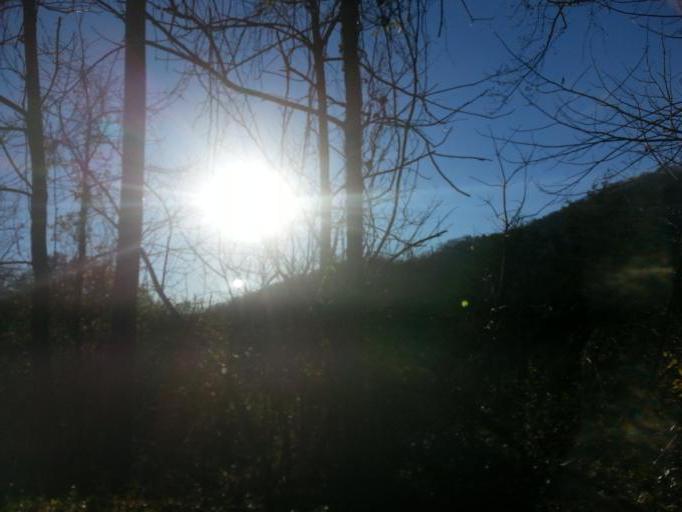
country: US
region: Tennessee
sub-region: Anderson County
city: Oak Ridge
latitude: 36.0900
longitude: -84.2386
